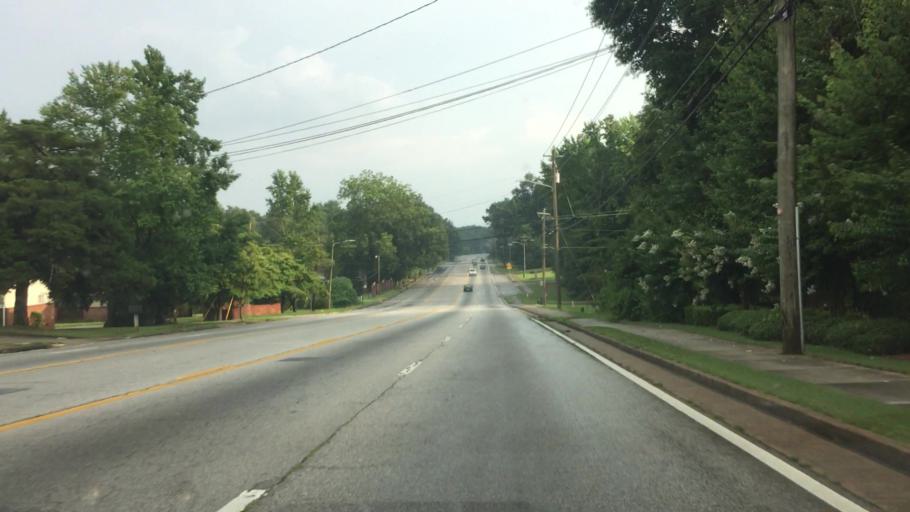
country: US
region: Georgia
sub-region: DeKalb County
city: Candler-McAfee
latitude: 33.7303
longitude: -84.2141
